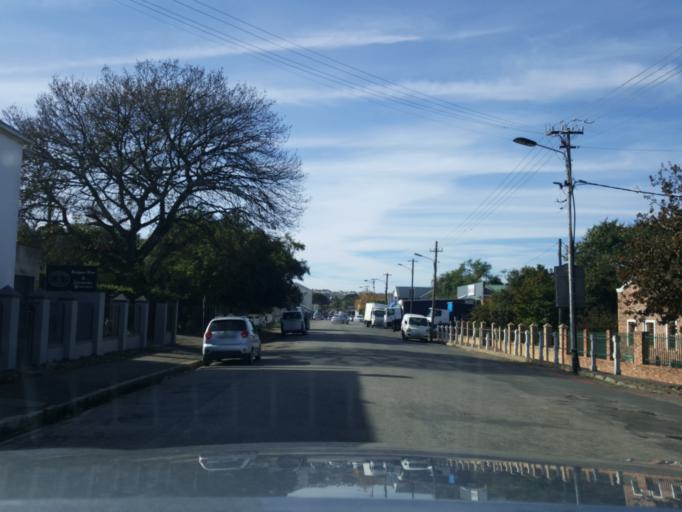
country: ZA
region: Eastern Cape
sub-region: Cacadu District Municipality
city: Grahamstown
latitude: -33.3088
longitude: 26.5206
